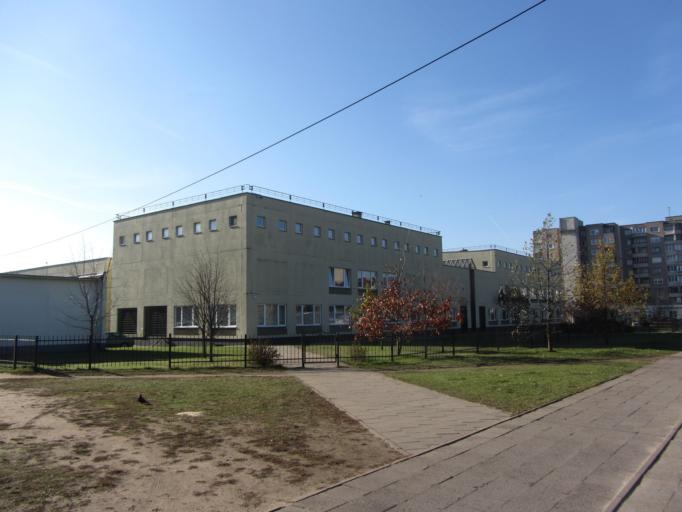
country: LT
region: Vilnius County
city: Pilaite
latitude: 54.7065
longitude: 25.1821
